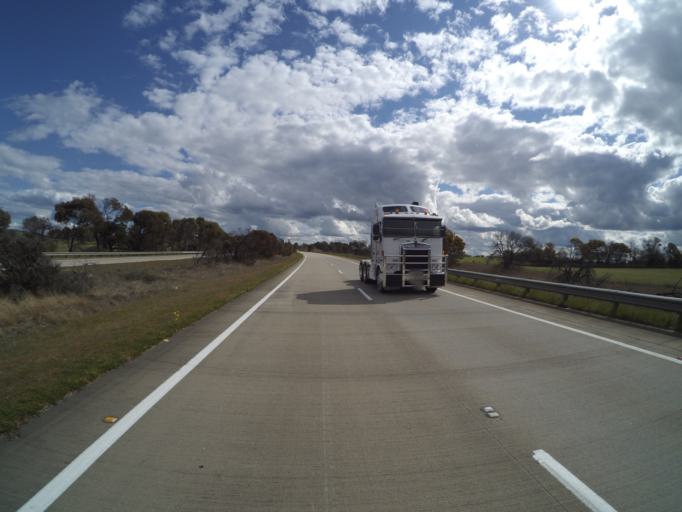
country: AU
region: New South Wales
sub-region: Yass Valley
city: Murrumbateman
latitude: -34.7864
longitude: 149.1823
